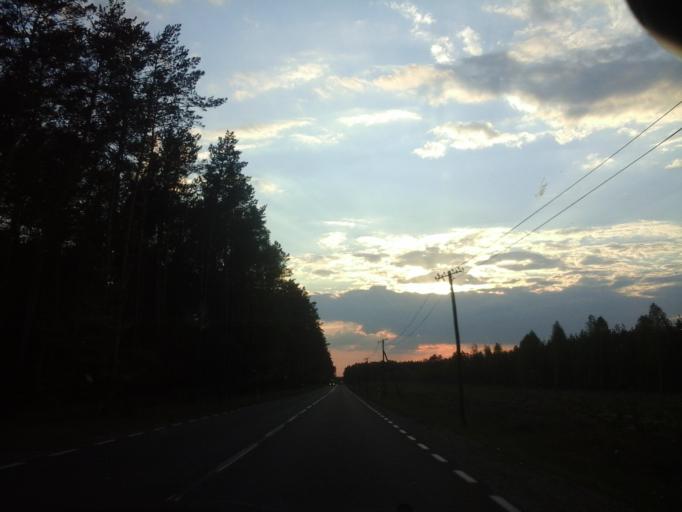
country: PL
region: West Pomeranian Voivodeship
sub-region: Powiat choszczenski
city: Drawno
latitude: 53.3007
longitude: 15.8048
